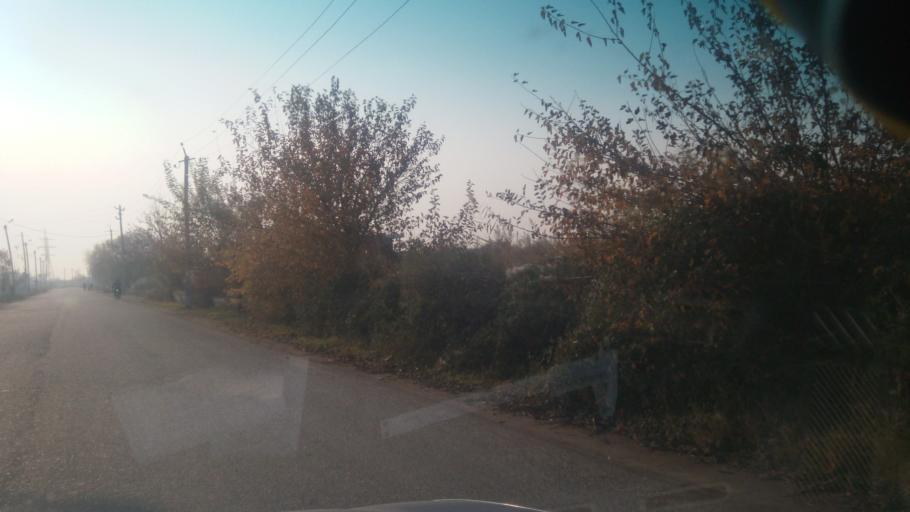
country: UZ
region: Sirdaryo
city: Guliston
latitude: 40.5171
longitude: 68.7744
